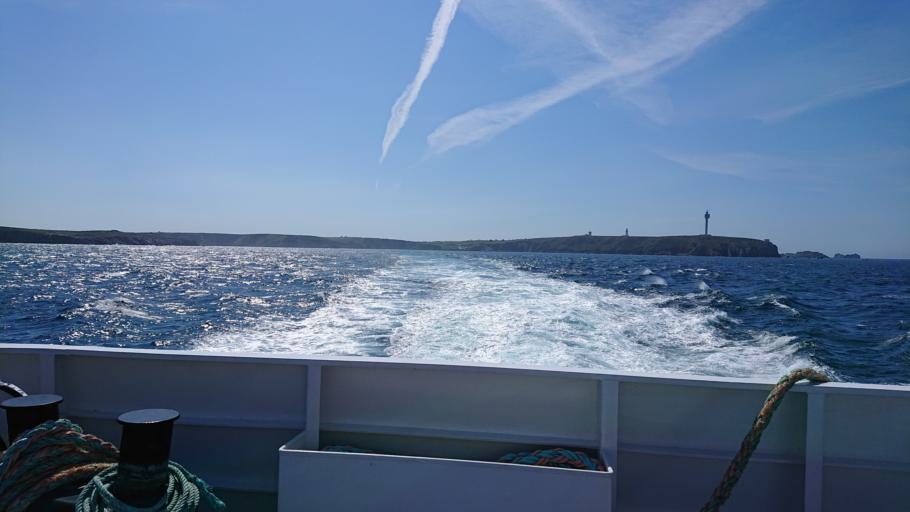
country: FR
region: Brittany
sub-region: Departement du Finistere
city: Porspoder
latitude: 48.4705
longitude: -5.0280
